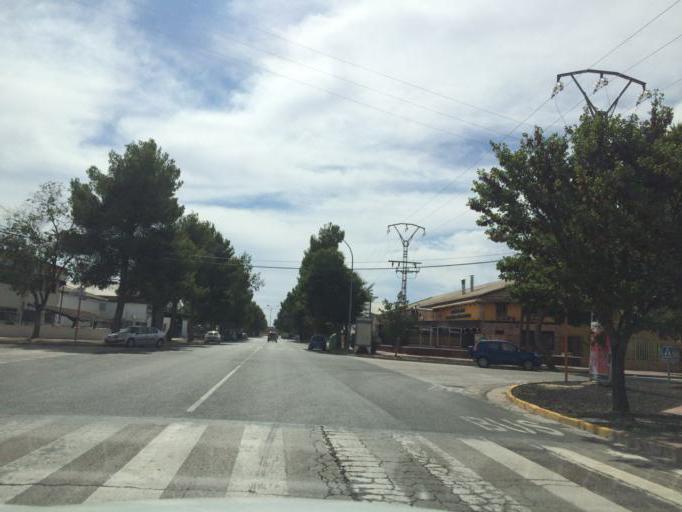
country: ES
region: Castille-La Mancha
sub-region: Provincia de Albacete
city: Albacete
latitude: 39.0108
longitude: -1.8839
